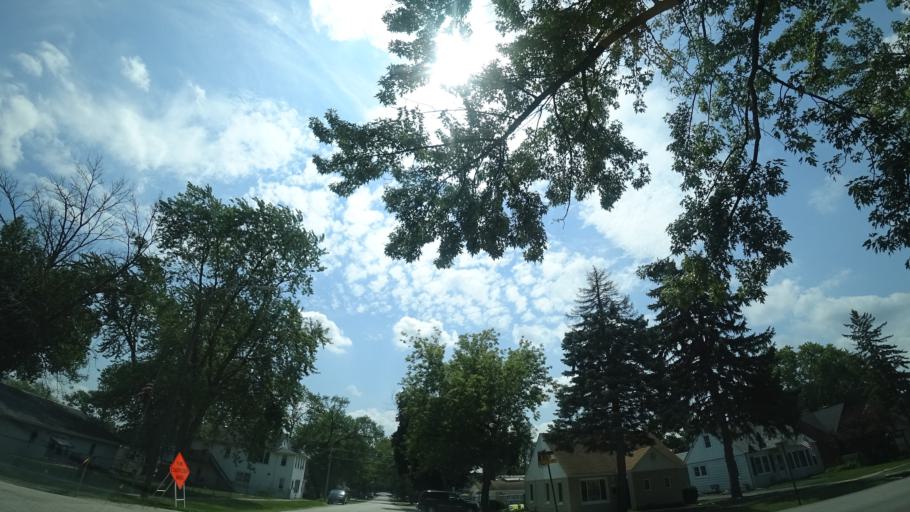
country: US
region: Illinois
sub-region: Cook County
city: Worth
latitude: 41.6855
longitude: -87.7950
